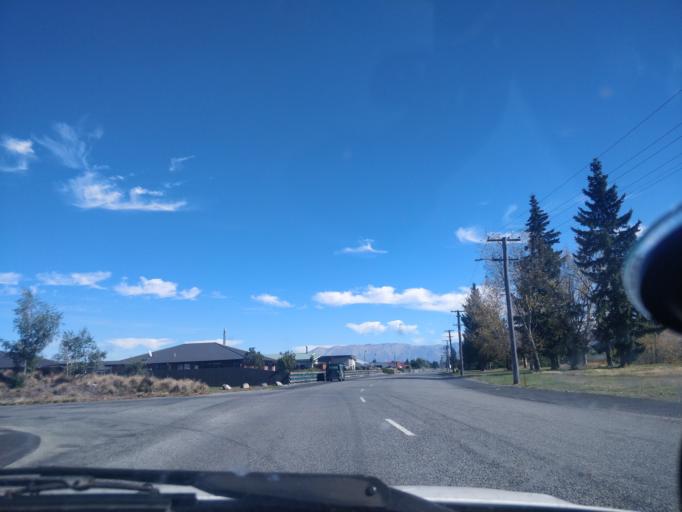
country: NZ
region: Canterbury
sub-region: Timaru District
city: Pleasant Point
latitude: -44.2641
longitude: 170.0980
